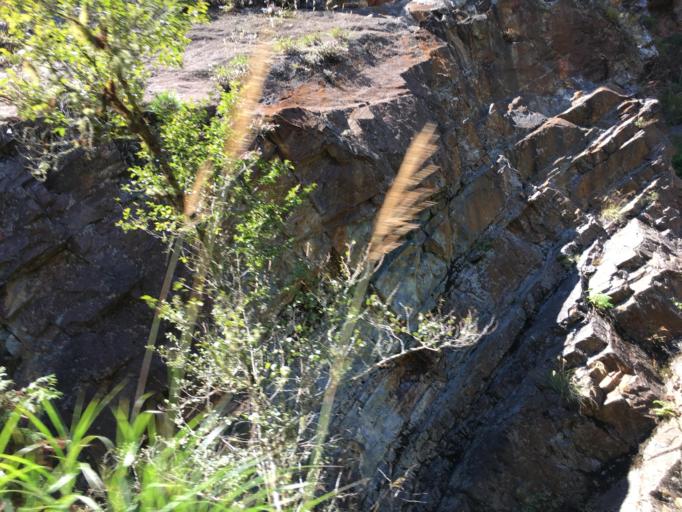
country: TW
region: Taiwan
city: Daxi
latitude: 24.5487
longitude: 121.3989
